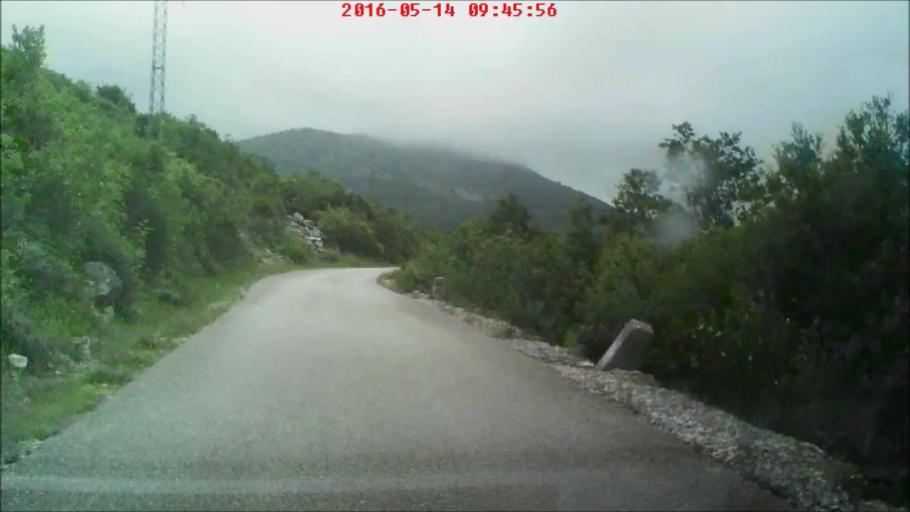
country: HR
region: Dubrovacko-Neretvanska
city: Podgora
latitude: 42.7802
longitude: 17.9125
